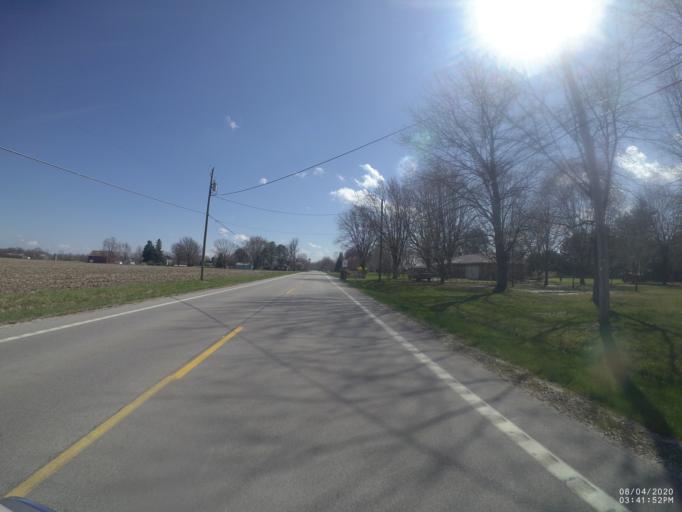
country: US
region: Ohio
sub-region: Sandusky County
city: Stony Prairie
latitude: 41.2553
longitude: -83.2357
